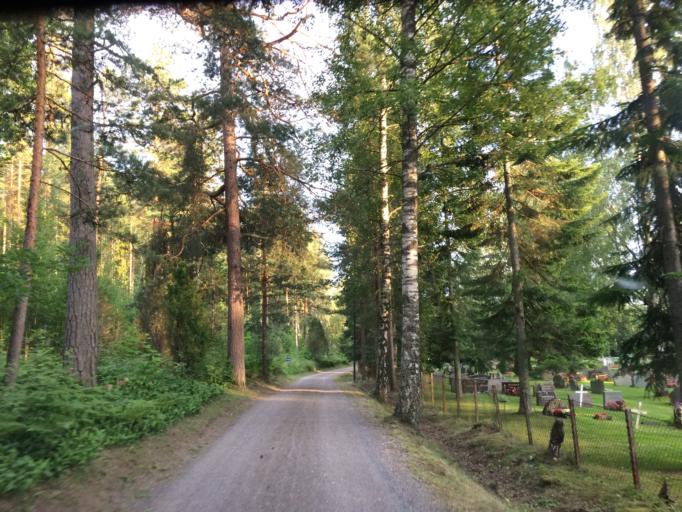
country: FI
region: Haeme
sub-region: Haemeenlinna
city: Janakkala
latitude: 60.8940
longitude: 24.5997
